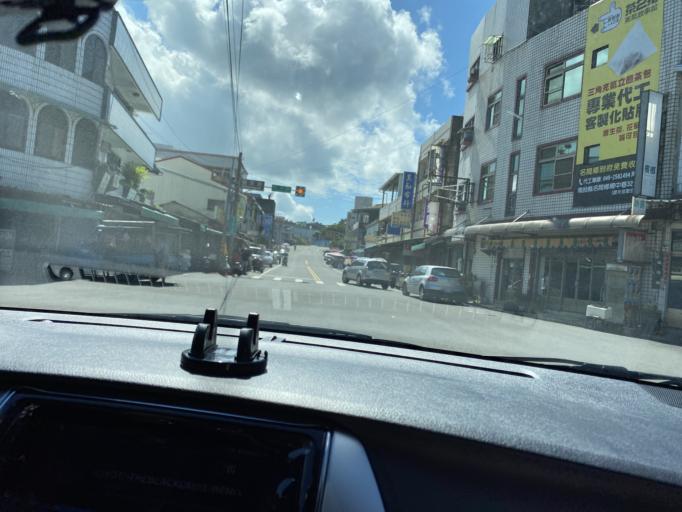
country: TW
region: Taiwan
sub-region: Nantou
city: Nantou
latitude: 23.8348
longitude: 120.6348
